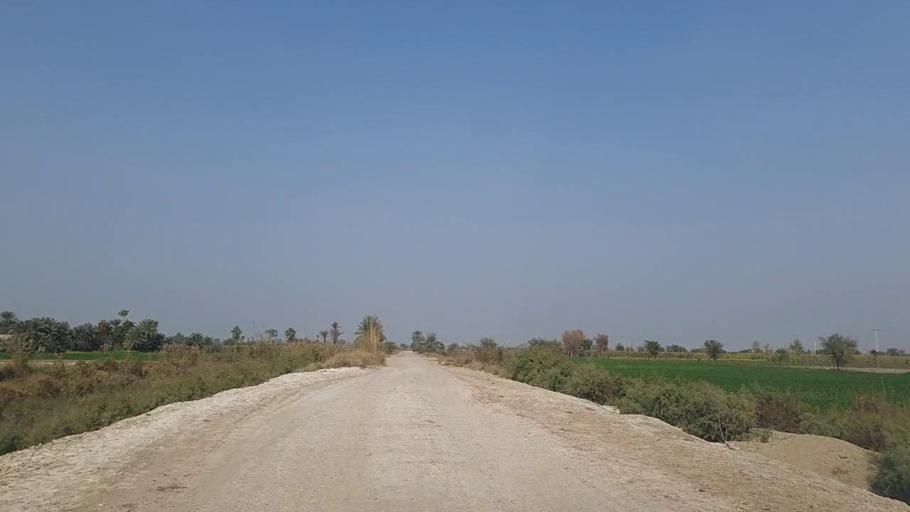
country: PK
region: Sindh
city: Daur
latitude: 26.4815
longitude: 68.4513
